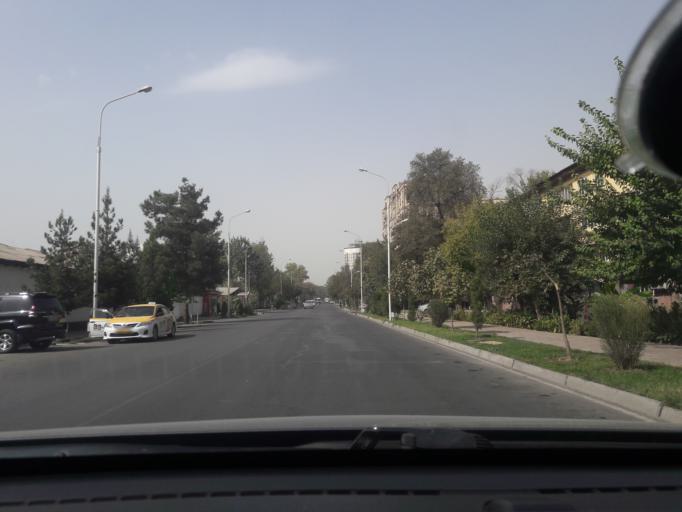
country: TJ
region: Dushanbe
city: Dushanbe
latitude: 38.5641
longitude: 68.7608
